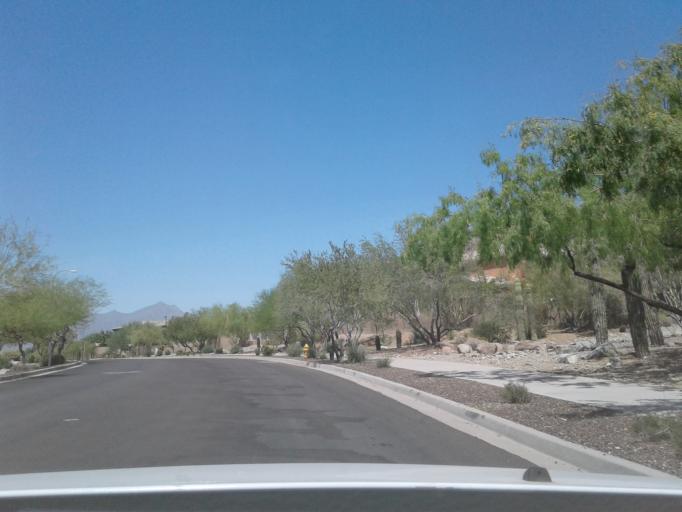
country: US
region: Arizona
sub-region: Maricopa County
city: Laveen
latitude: 33.2967
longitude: -112.1226
